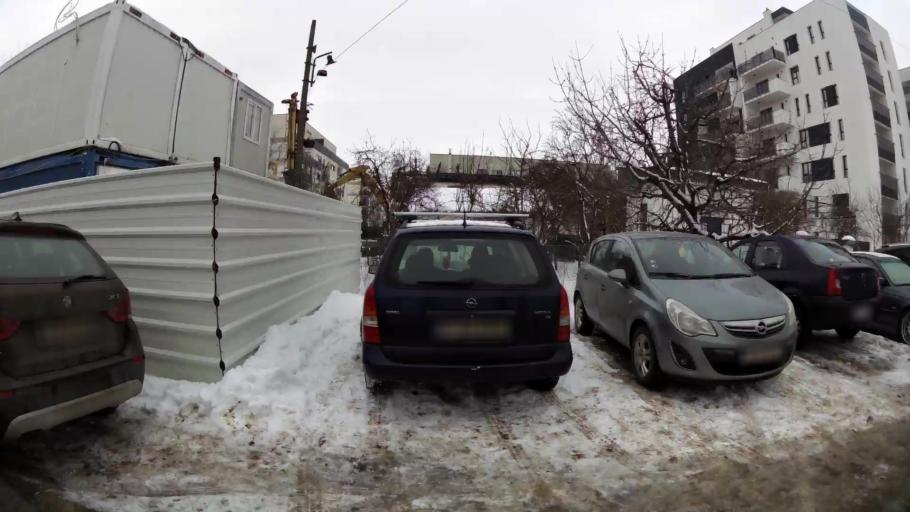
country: RO
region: Ilfov
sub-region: Comuna Otopeni
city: Otopeni
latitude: 44.5132
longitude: 26.1036
